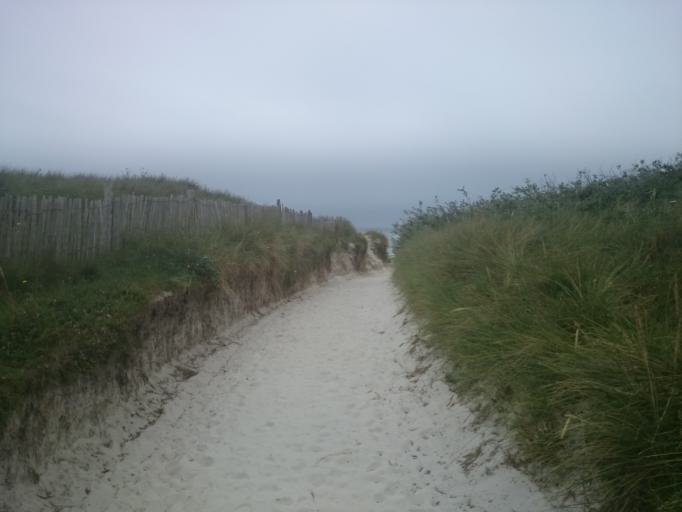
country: FR
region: Brittany
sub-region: Departement du Finistere
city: Saint-Pabu
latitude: 48.5766
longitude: -4.6324
